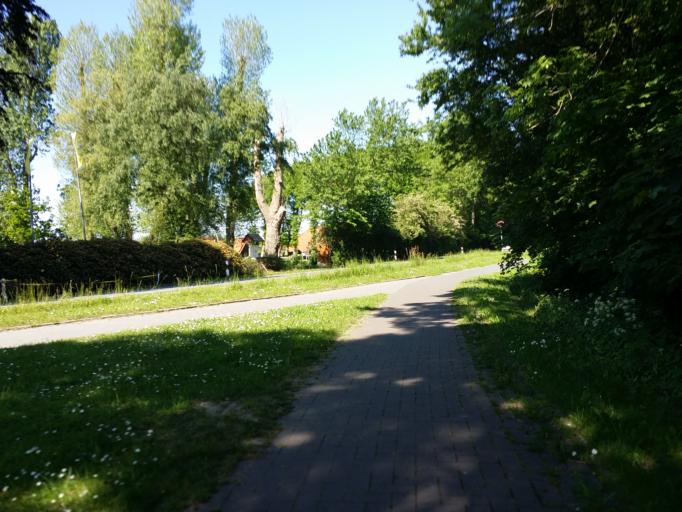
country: DE
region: Lower Saxony
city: Esens
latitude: 53.6494
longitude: 7.6204
